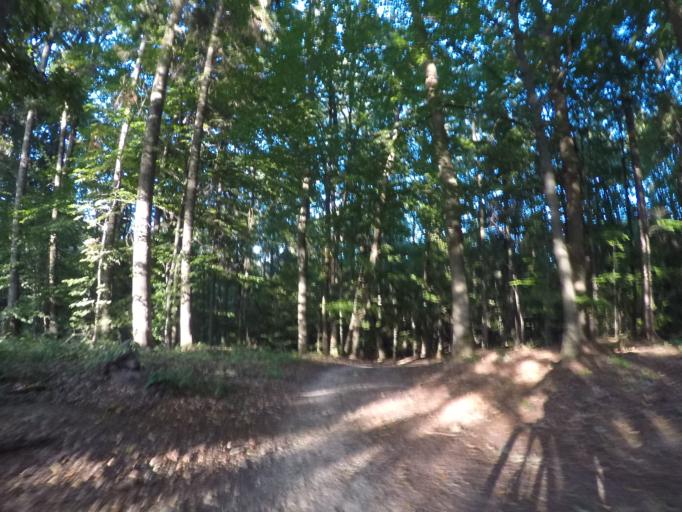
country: SK
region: Kosicky
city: Kosice
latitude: 48.7493
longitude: 21.1738
